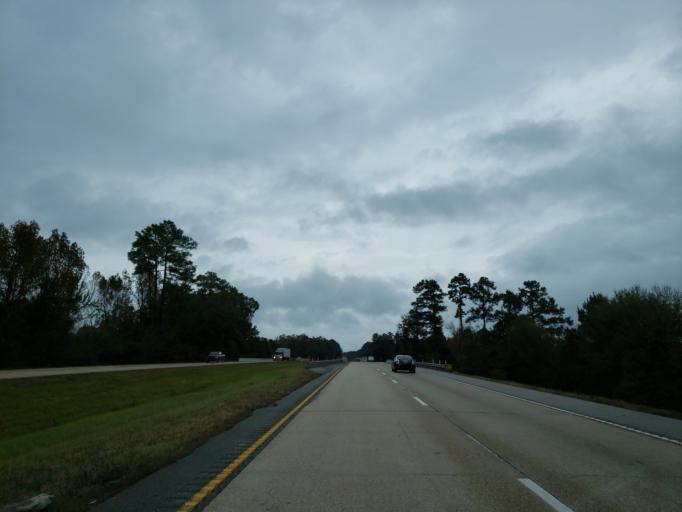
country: US
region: Mississippi
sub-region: Forrest County
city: Glendale
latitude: 31.4092
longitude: -89.3184
